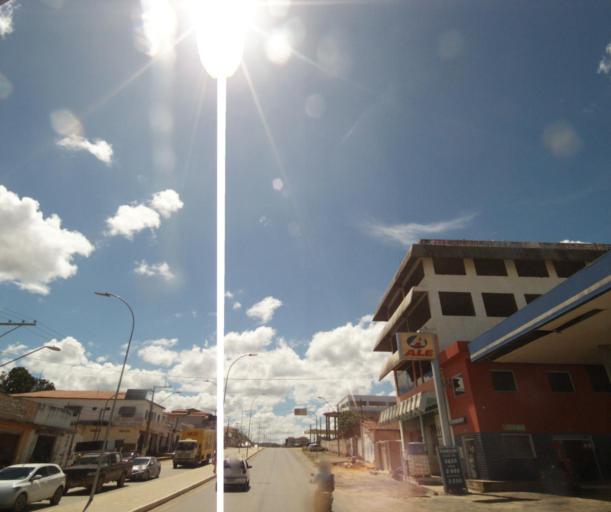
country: BR
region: Bahia
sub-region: Sao Felix Do Coribe
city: Santa Maria da Vitoria
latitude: -13.4059
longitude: -44.1911
